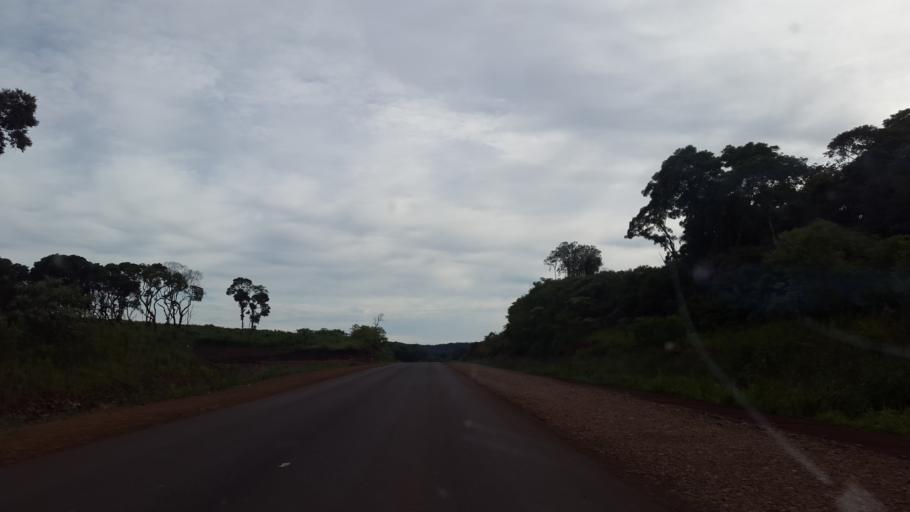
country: AR
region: Misiones
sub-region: Departamento de San Pedro
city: San Pedro
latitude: -26.4802
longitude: -53.8840
